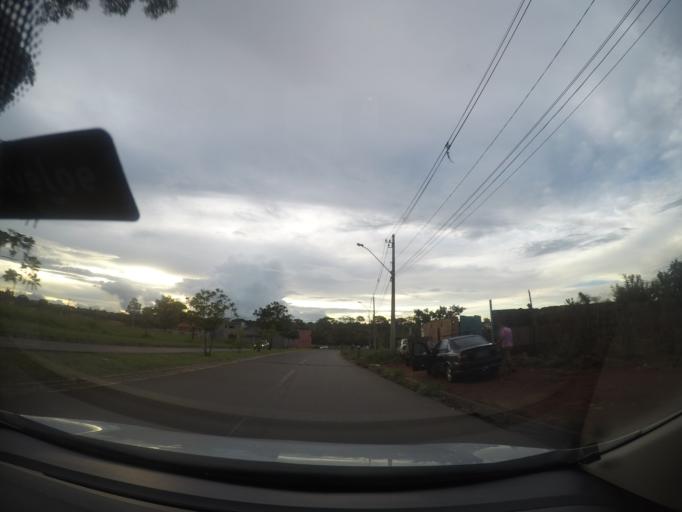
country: BR
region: Goias
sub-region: Goiania
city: Goiania
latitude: -16.7317
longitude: -49.3667
